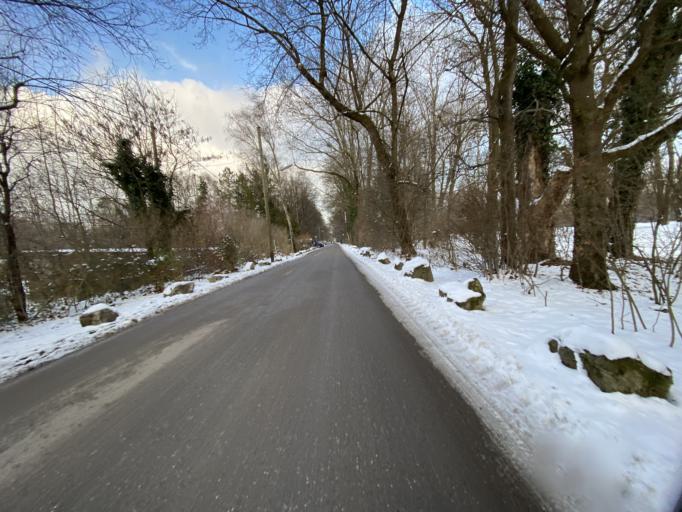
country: DE
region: Bavaria
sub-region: Upper Bavaria
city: Bogenhausen
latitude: 48.1618
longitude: 11.6046
